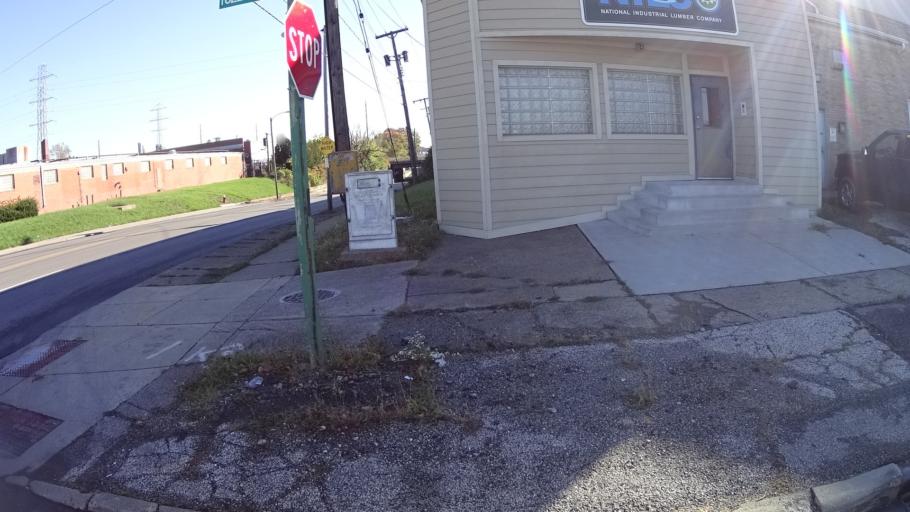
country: US
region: Ohio
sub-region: Lorain County
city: Lorain
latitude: 41.4450
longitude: -82.1583
